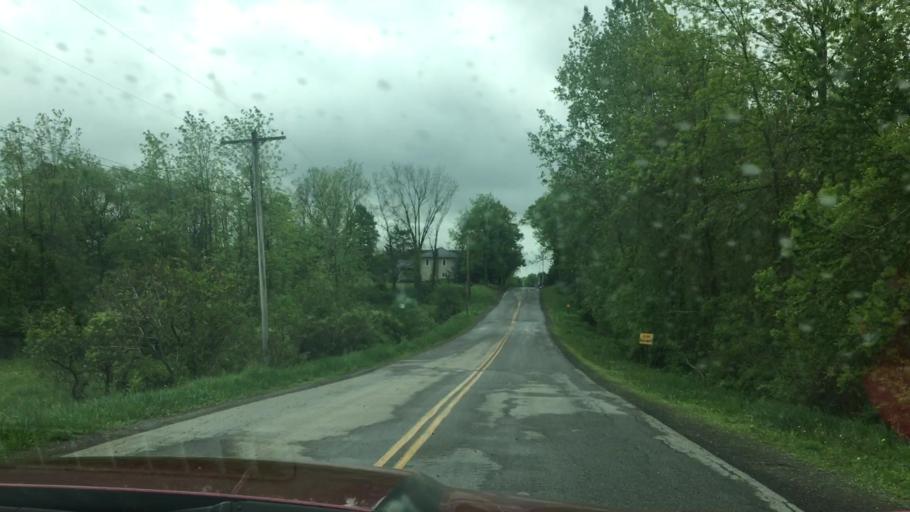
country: US
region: New York
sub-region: Genesee County
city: Batavia
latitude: 43.0825
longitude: -78.1395
